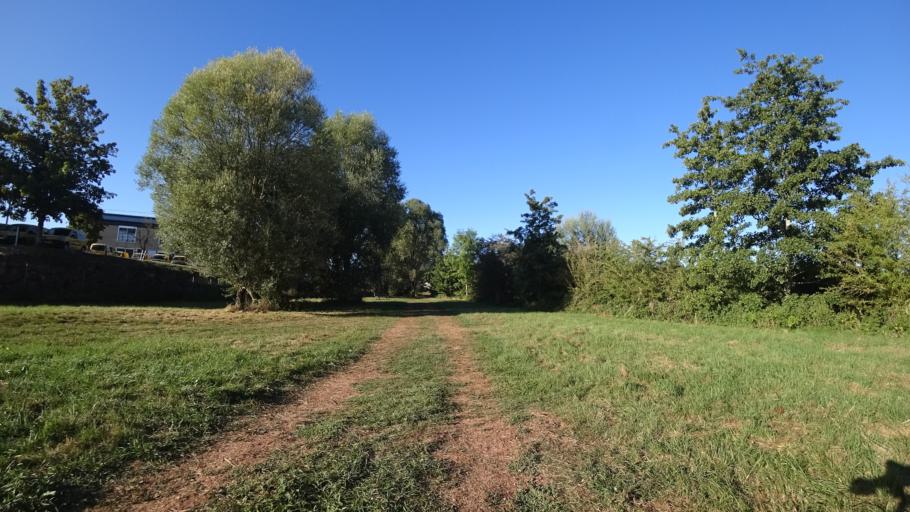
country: FR
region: Midi-Pyrenees
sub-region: Departement de l'Aveyron
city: Rodez
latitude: 44.3714
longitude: 2.5815
